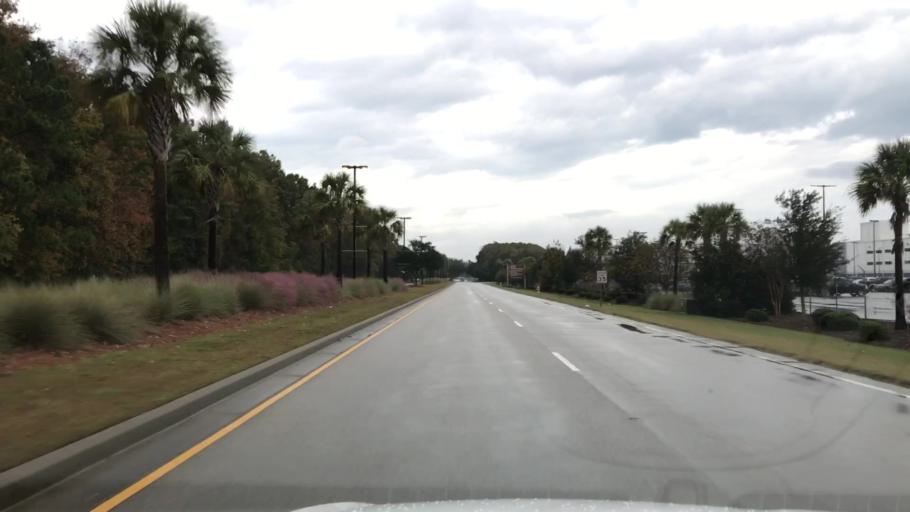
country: US
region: South Carolina
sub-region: Berkeley County
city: Hanahan
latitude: 32.8752
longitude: -80.0380
